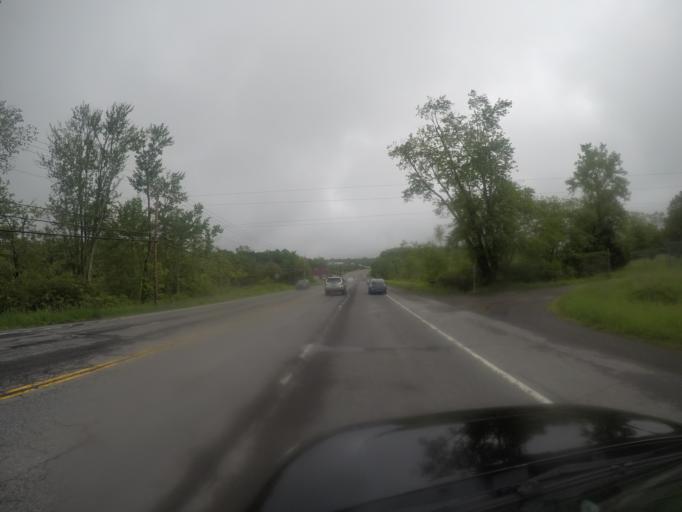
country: US
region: New York
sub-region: Ulster County
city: West Hurley
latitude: 41.9771
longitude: -74.0840
